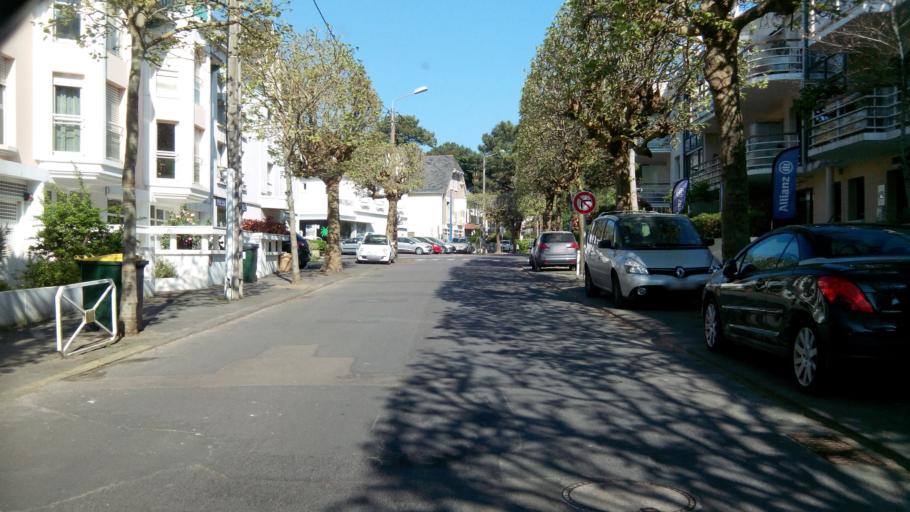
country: FR
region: Pays de la Loire
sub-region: Departement de la Loire-Atlantique
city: La Baule-Escoublac
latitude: 47.2815
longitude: -2.3692
